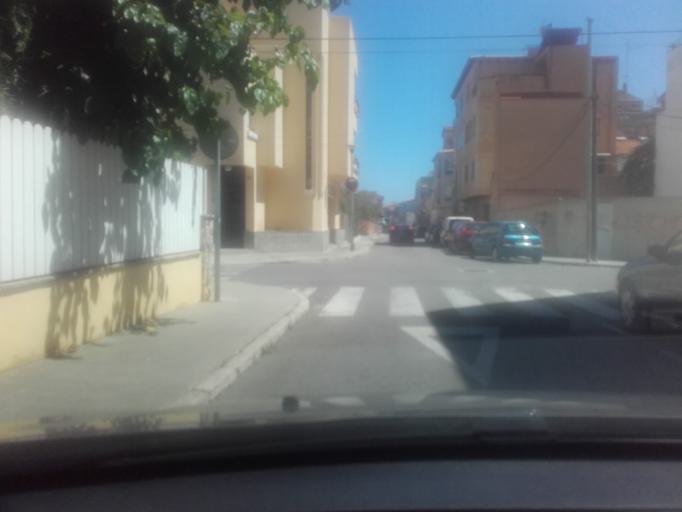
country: ES
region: Catalonia
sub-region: Provincia de Tarragona
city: El Vendrell
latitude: 41.2194
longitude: 1.5285
